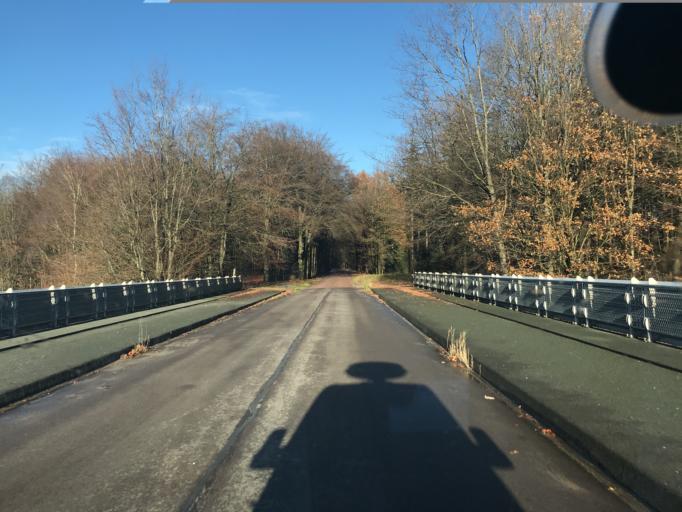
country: NL
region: Gelderland
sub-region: Gemeente Apeldoorn
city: Uddel
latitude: 52.1910
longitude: 5.8444
